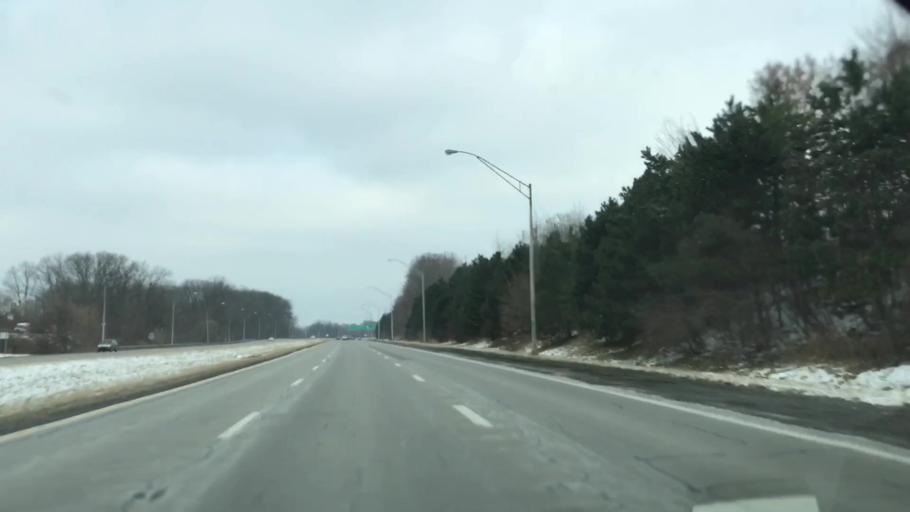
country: US
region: Ohio
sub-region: Mahoning County
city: Struthers
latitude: 41.0524
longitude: -80.6293
